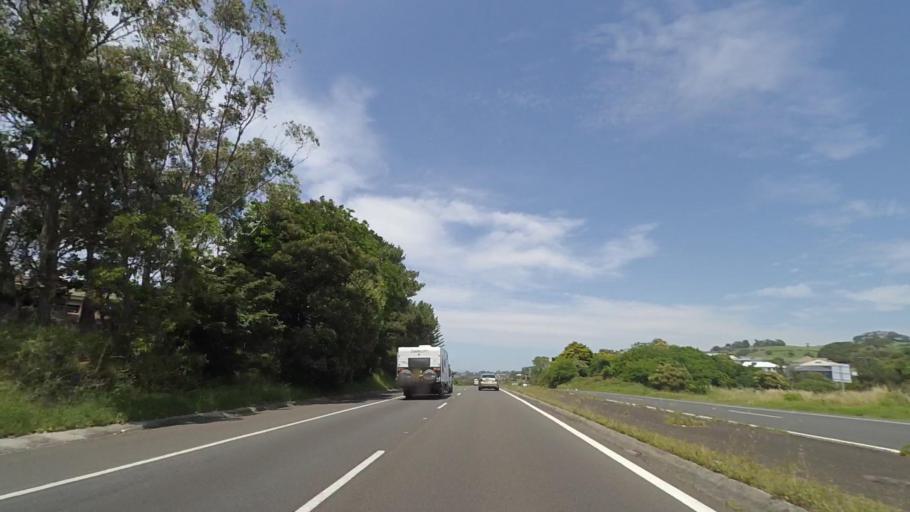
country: AU
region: New South Wales
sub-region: Kiama
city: Kiama
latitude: -34.6743
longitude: 150.8429
